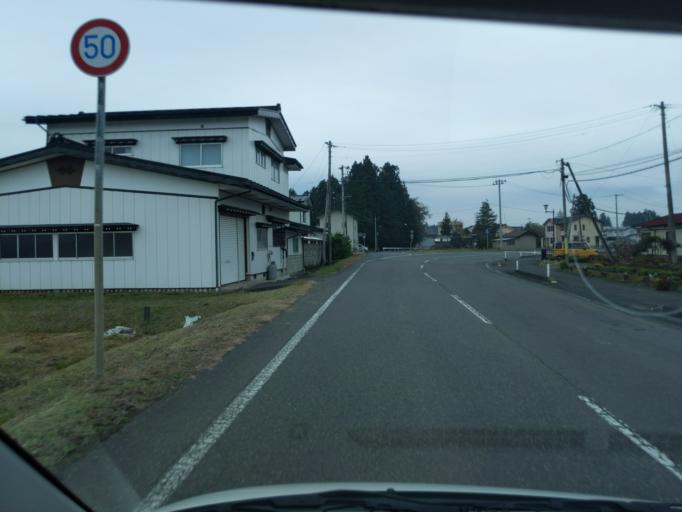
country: JP
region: Iwate
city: Mizusawa
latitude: 39.0988
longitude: 141.0845
